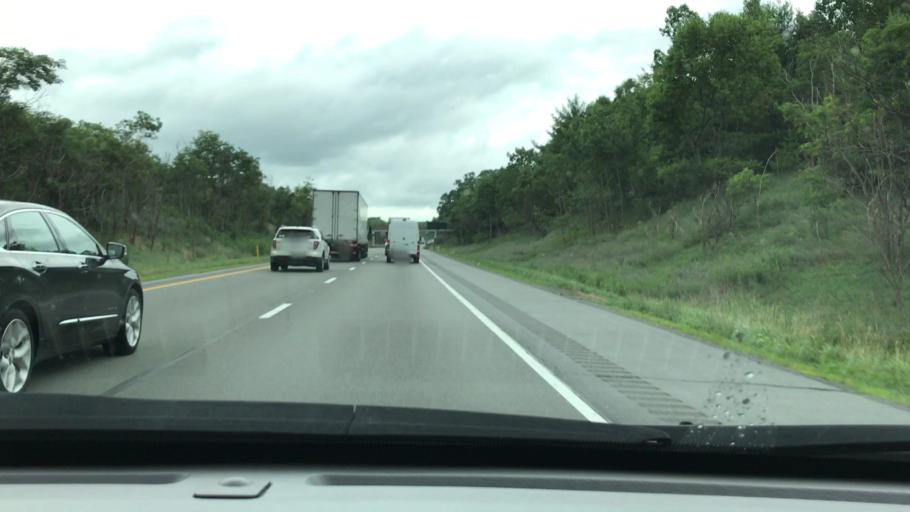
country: US
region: Pennsylvania
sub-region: Clearfield County
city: Clearfield
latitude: 41.0616
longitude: -78.4517
